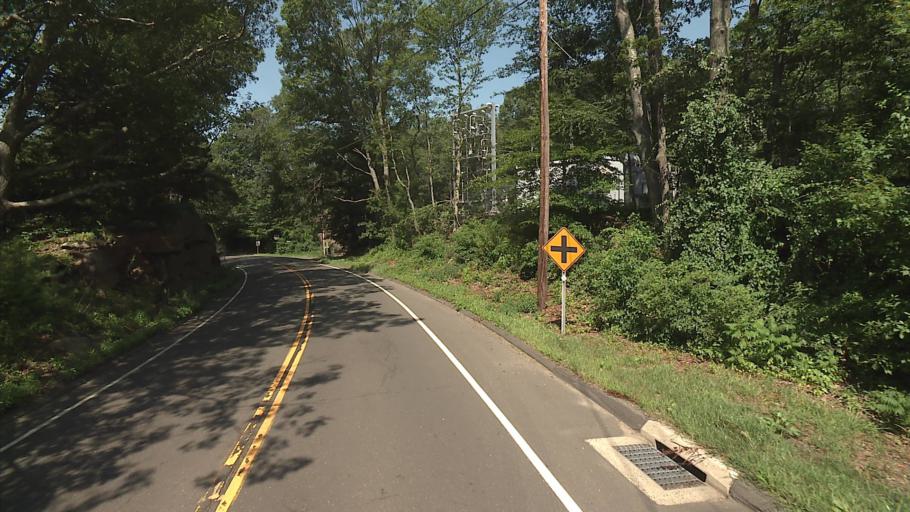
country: US
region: Connecticut
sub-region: New Haven County
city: Guilford
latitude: 41.2652
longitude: -72.7248
